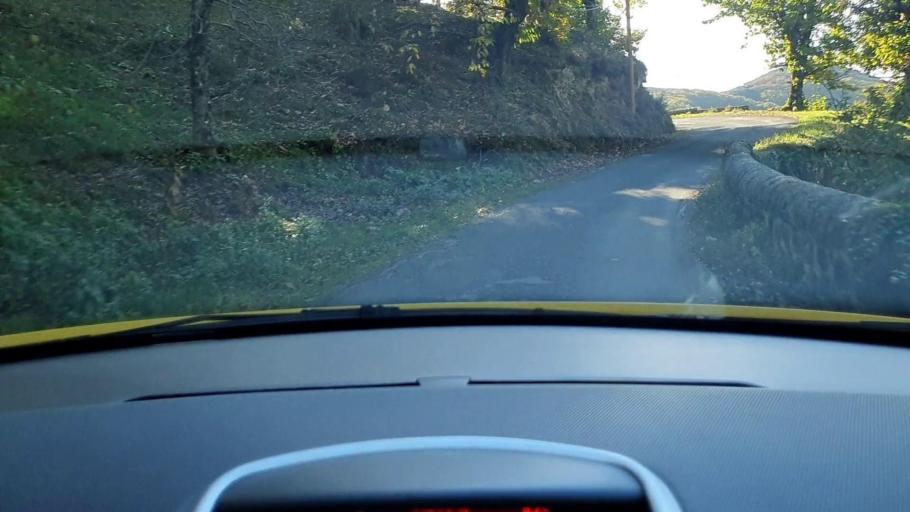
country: FR
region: Languedoc-Roussillon
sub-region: Departement du Gard
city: Sumene
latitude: 44.0177
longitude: 3.7772
